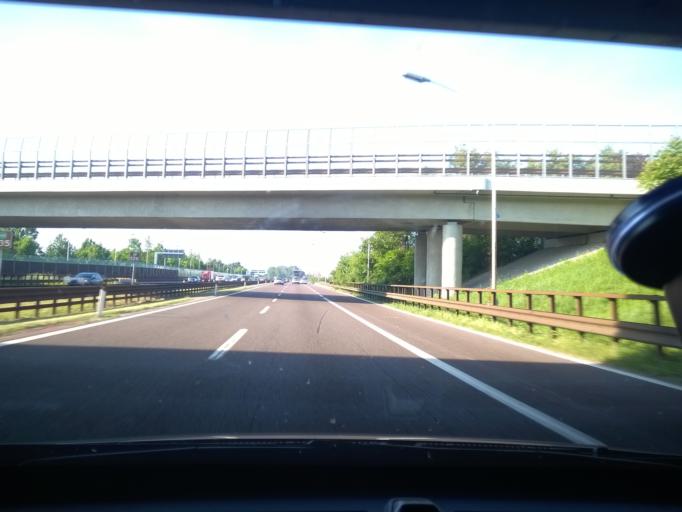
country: IT
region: Emilia-Romagna
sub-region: Provincia di Modena
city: Santa Croce Scuole
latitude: 44.7643
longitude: 10.8440
